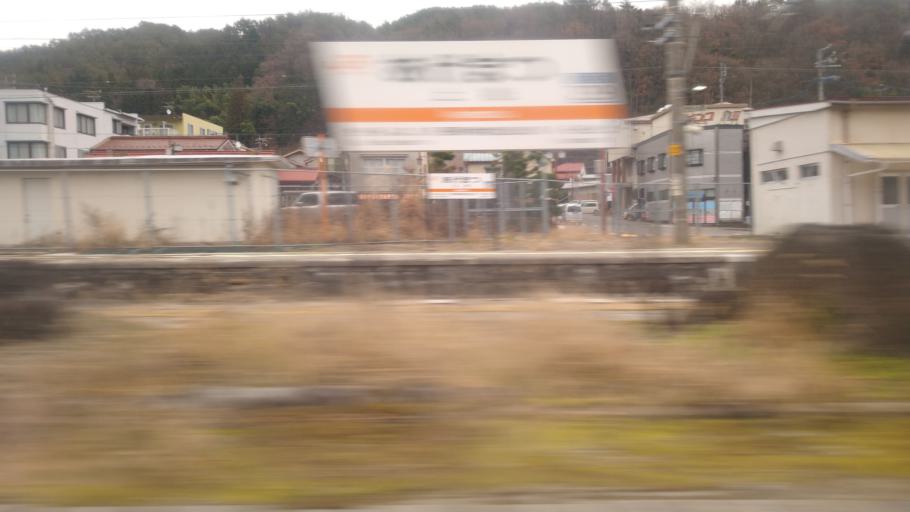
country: JP
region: Nagano
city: Ina
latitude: 35.7844
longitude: 137.6932
